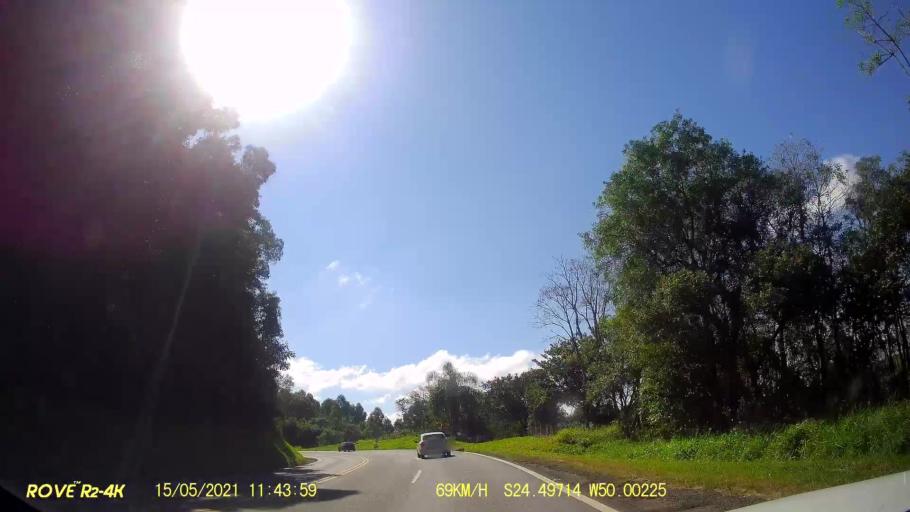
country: BR
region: Parana
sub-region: Pirai Do Sul
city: Pirai do Sul
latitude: -24.4972
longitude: -50.0023
